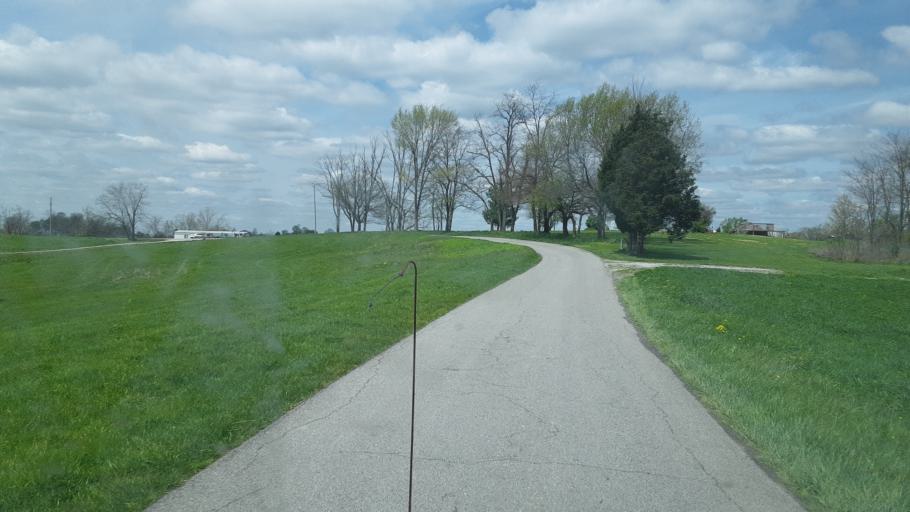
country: US
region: Kentucky
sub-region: Gallatin County
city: Warsaw
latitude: 38.6744
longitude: -84.8123
